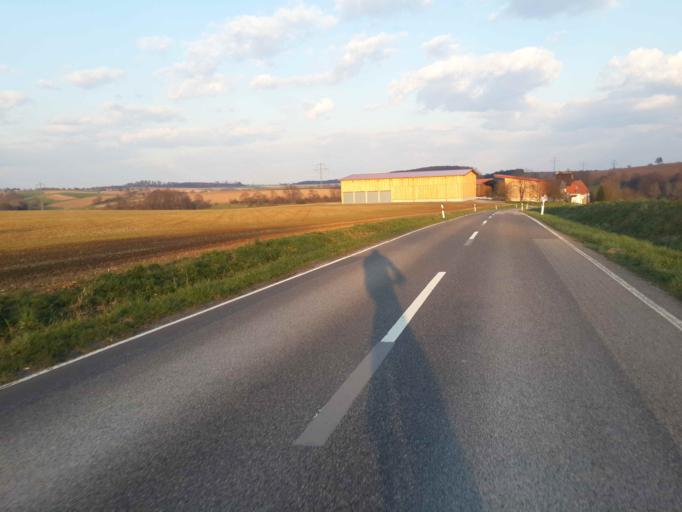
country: DE
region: Baden-Wuerttemberg
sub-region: Regierungsbezirk Stuttgart
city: Kirchardt
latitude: 49.2441
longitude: 8.9575
